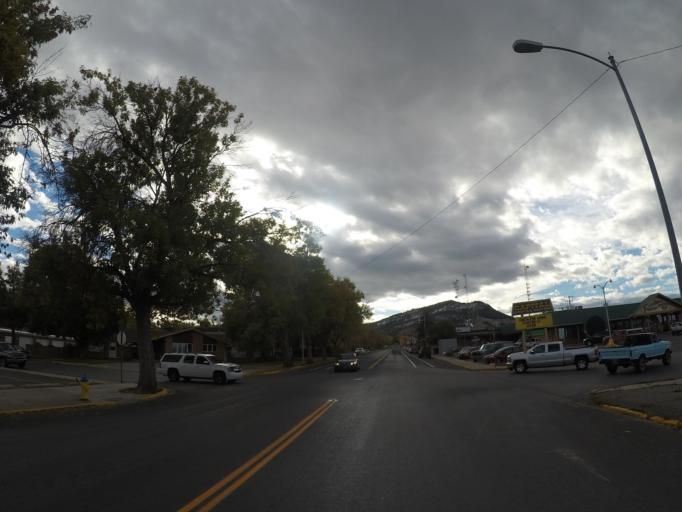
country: US
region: Montana
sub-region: Lewis and Clark County
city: Helena
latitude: 46.5973
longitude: -112.0230
